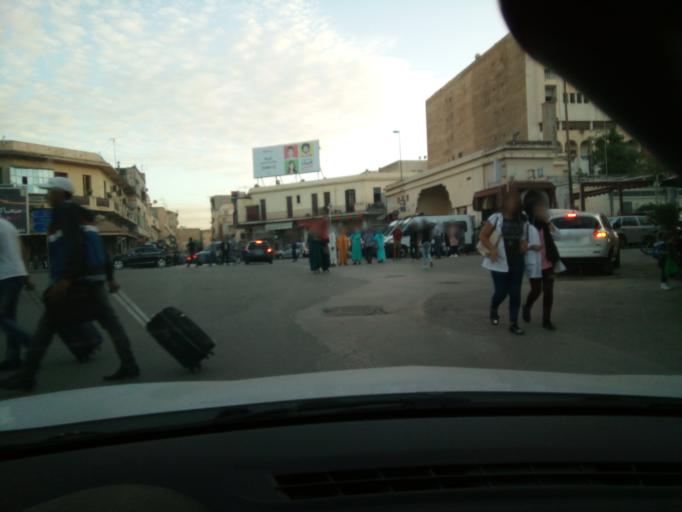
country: MA
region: Fes-Boulemane
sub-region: Fes
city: Fes
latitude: 34.0324
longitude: -4.9951
